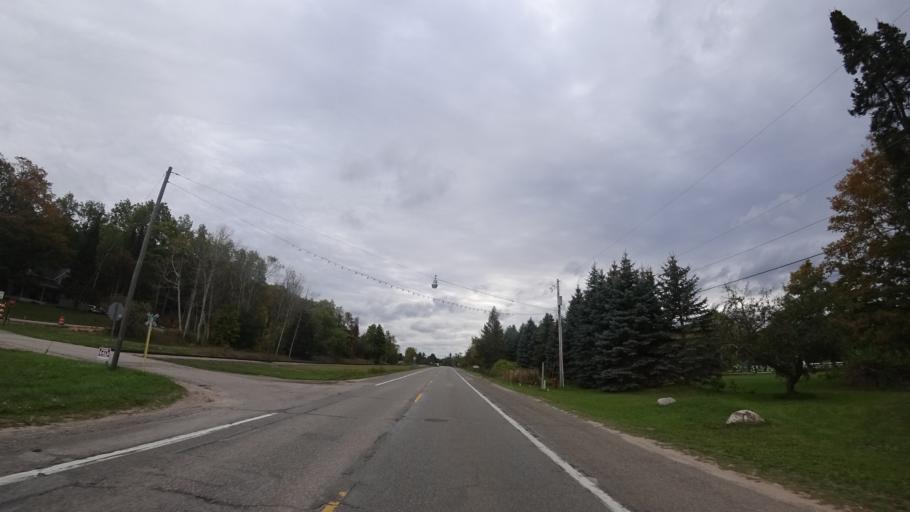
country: US
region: Michigan
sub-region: Charlevoix County
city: Boyne City
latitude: 45.1643
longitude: -84.9178
